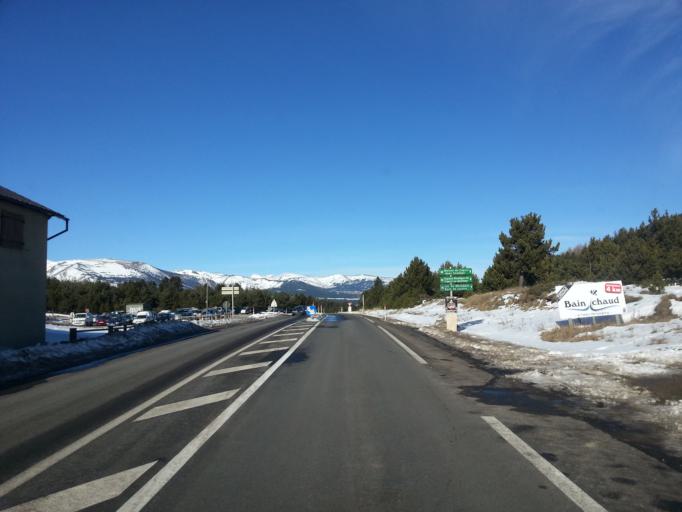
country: ES
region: Catalonia
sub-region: Provincia de Girona
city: Llivia
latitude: 42.5481
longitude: 2.1142
